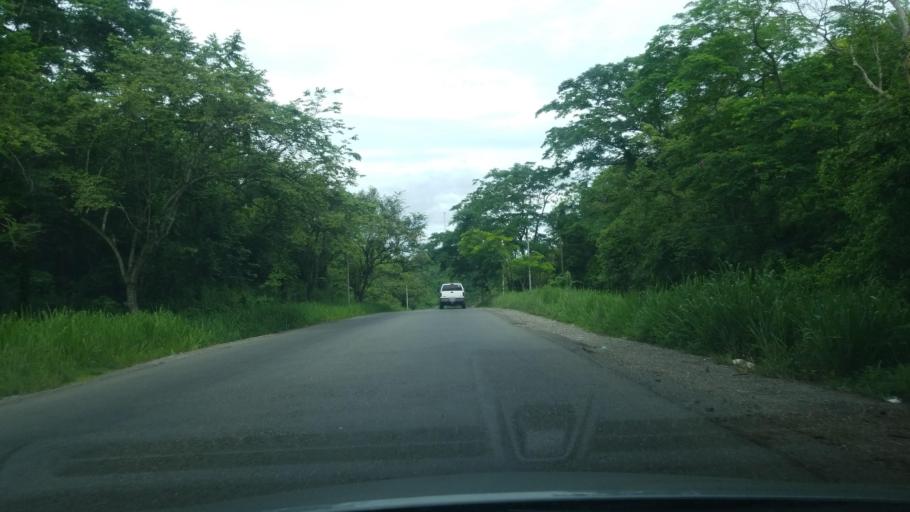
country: HN
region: Santa Barbara
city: Camalote
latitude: 15.3313
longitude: -88.2991
